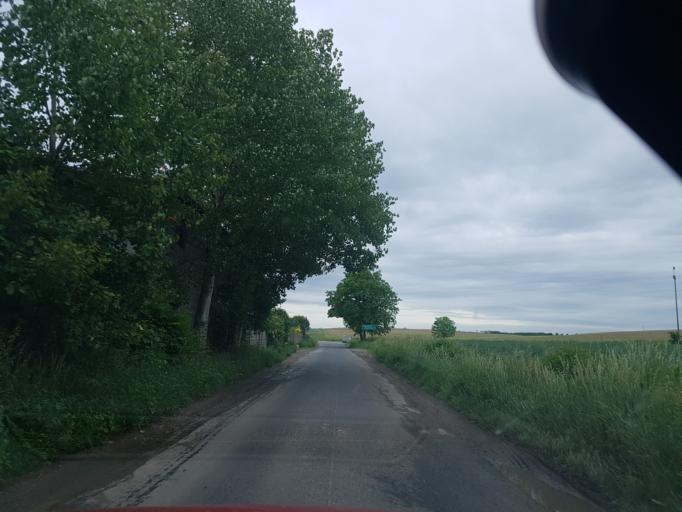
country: PL
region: Lower Silesian Voivodeship
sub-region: Powiat wroclawski
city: Katy Wroclawskie
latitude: 50.9806
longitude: 16.7740
